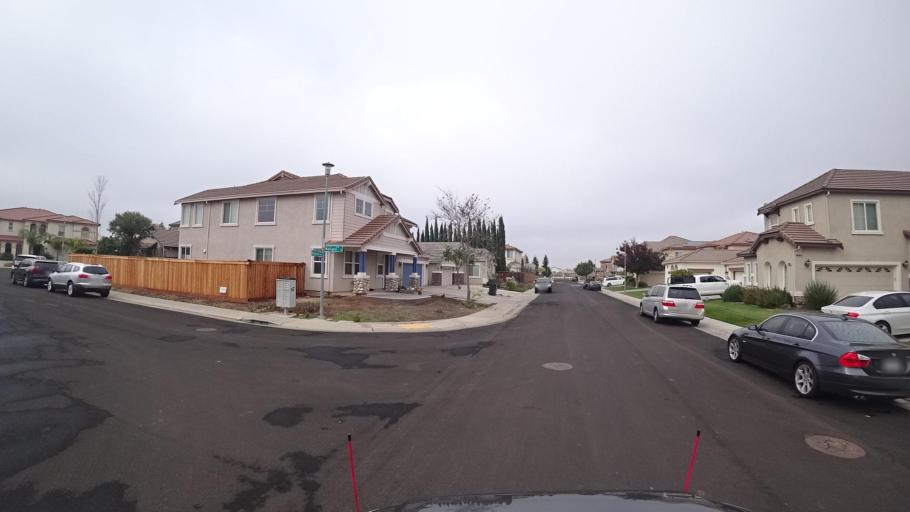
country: US
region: California
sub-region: Sacramento County
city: Elk Grove
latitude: 38.3945
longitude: -121.3453
